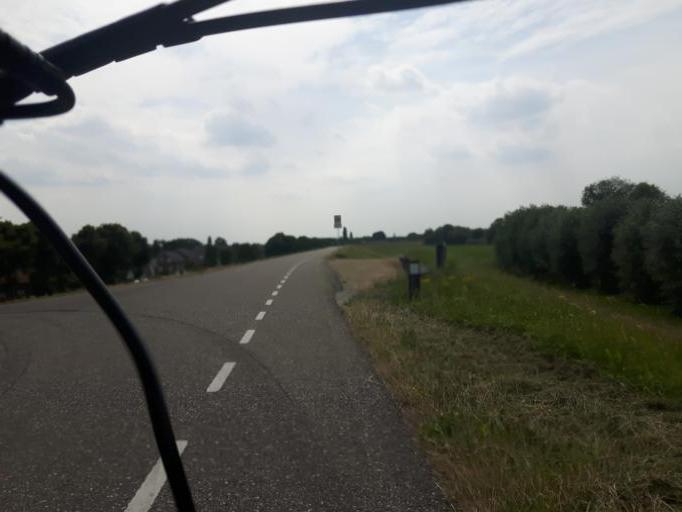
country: NL
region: Gelderland
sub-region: Gemeente Zaltbommel
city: Zaltbommel
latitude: 51.8075
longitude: 5.2234
